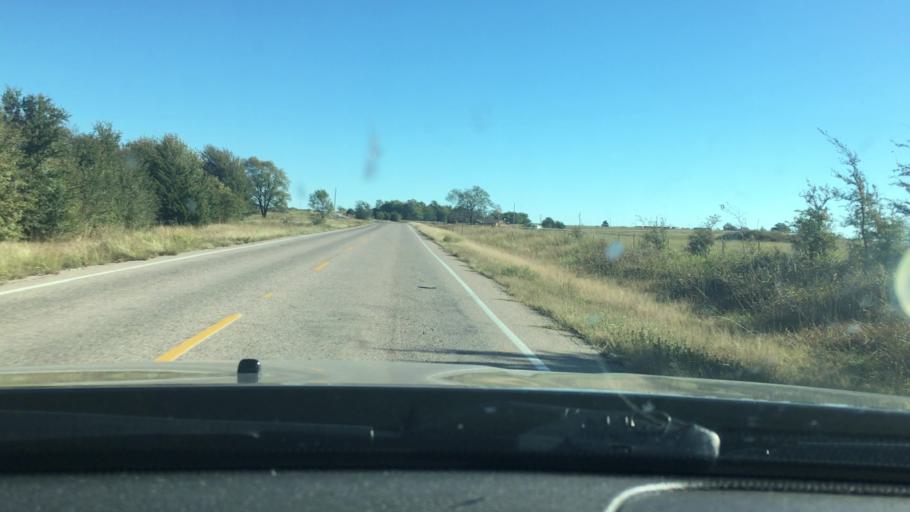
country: US
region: Oklahoma
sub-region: Marshall County
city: Madill
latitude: 34.1128
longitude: -96.7403
